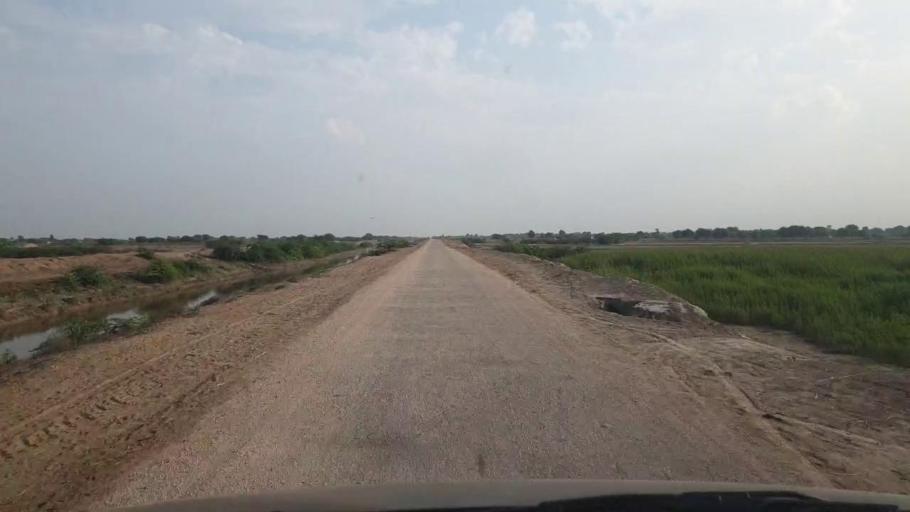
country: PK
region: Sindh
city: Badin
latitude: 24.5429
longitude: 68.6733
